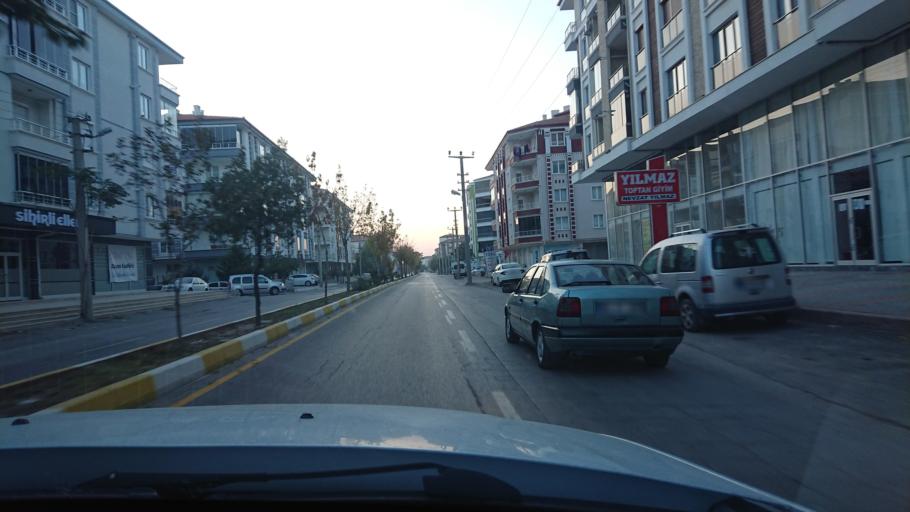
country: TR
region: Aksaray
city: Aksaray
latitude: 38.3605
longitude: 34.0189
